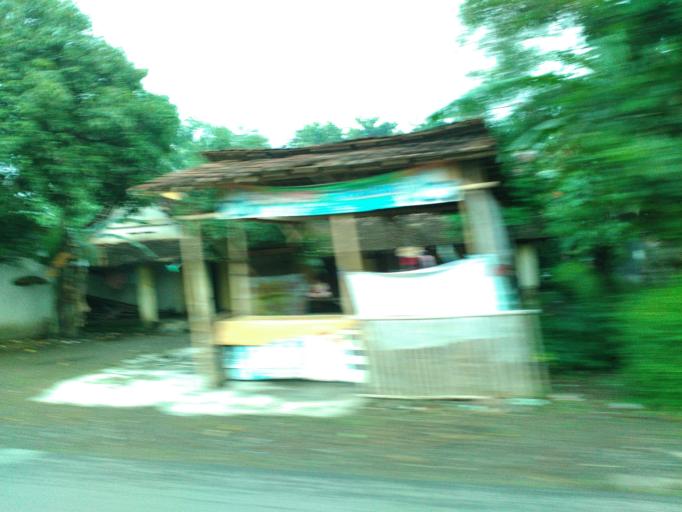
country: ID
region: Central Java
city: Ceper
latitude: -7.6529
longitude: 110.6890
